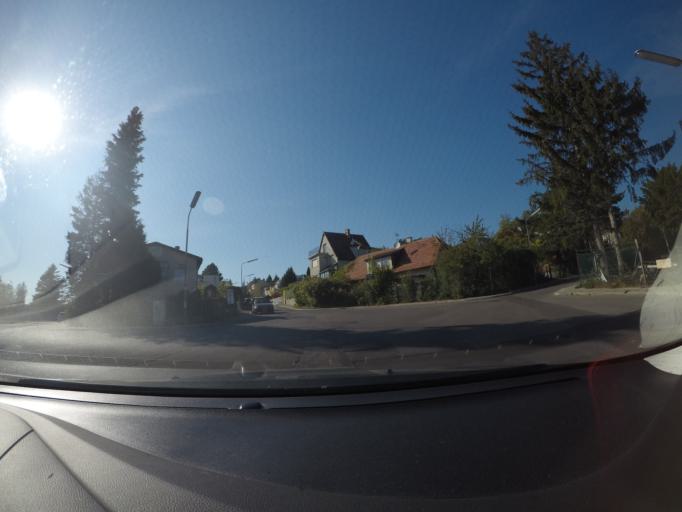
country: AT
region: Lower Austria
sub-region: Politischer Bezirk Modling
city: Perchtoldsdorf
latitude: 48.1673
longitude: 16.2641
